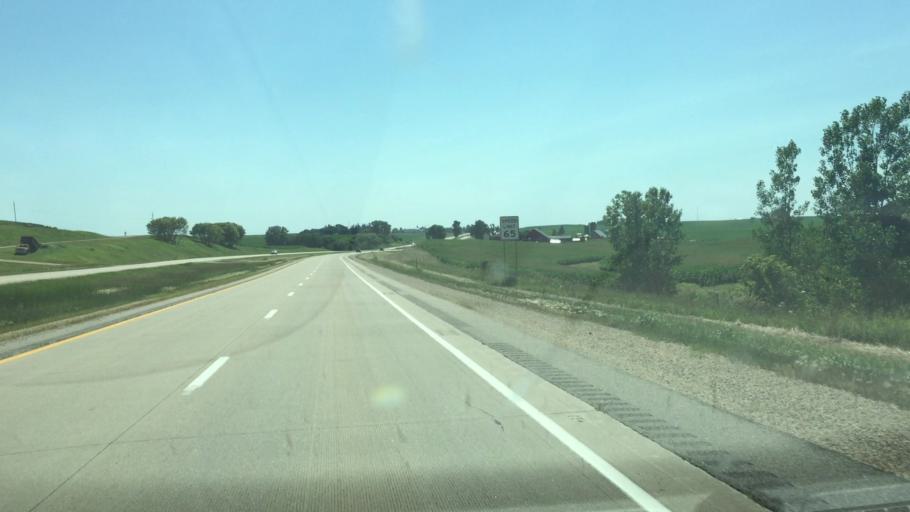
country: US
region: Iowa
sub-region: Dubuque County
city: Peosta
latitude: 42.3493
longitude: -90.8318
